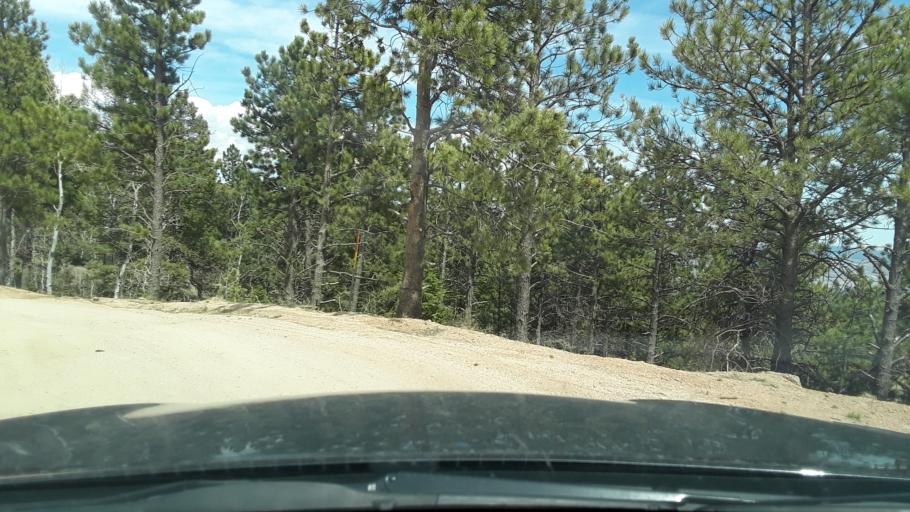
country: US
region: Colorado
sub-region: El Paso County
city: Palmer Lake
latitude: 39.0698
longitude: -104.9518
